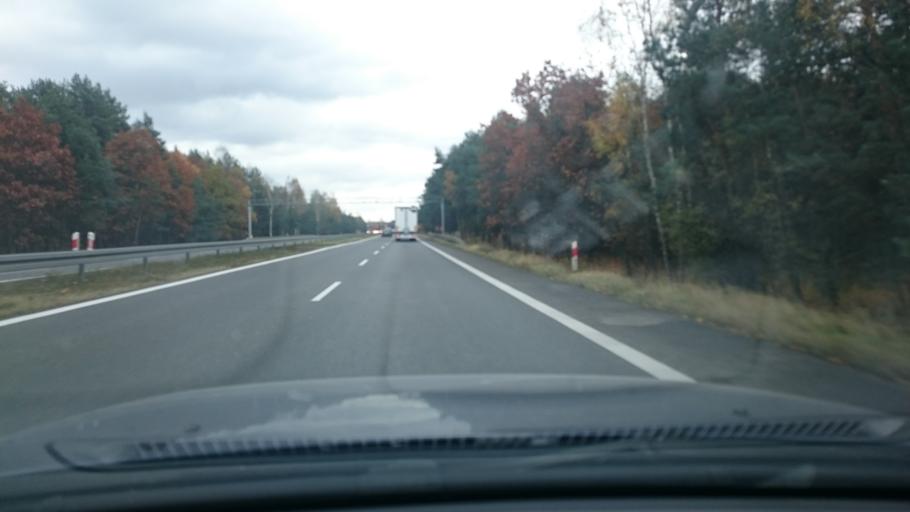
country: PL
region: Lesser Poland Voivodeship
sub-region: Powiat olkuski
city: Boleslaw
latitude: 50.2978
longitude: 19.4949
